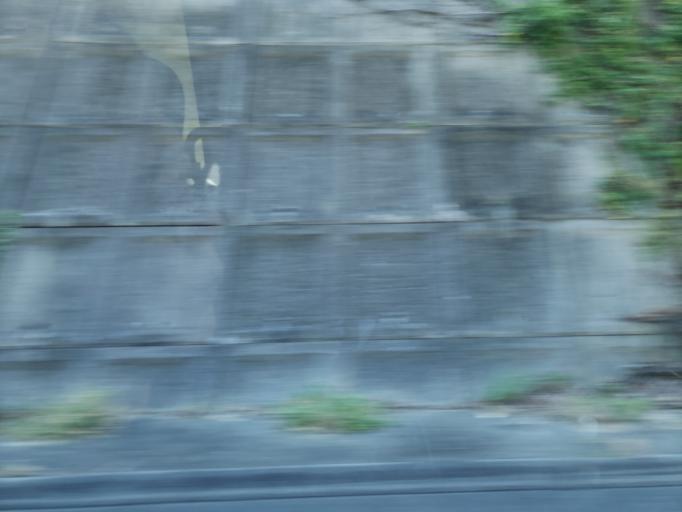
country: JP
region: Tokushima
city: Ishii
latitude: 34.1423
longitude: 134.4393
